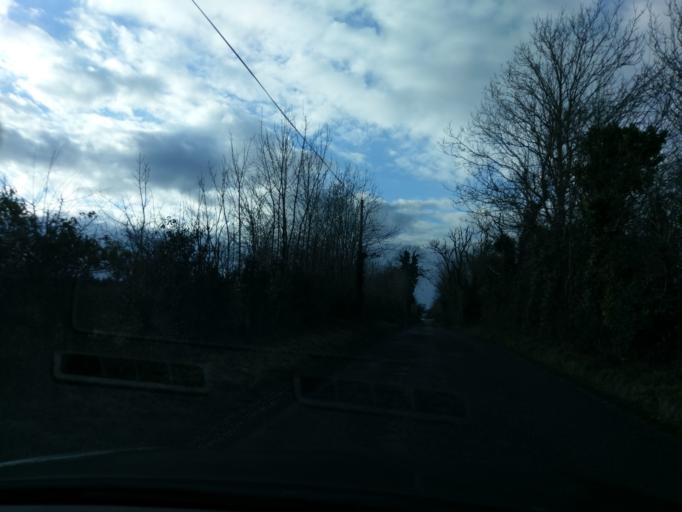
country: IE
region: Connaught
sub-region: County Galway
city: Athenry
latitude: 53.3929
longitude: -8.6143
